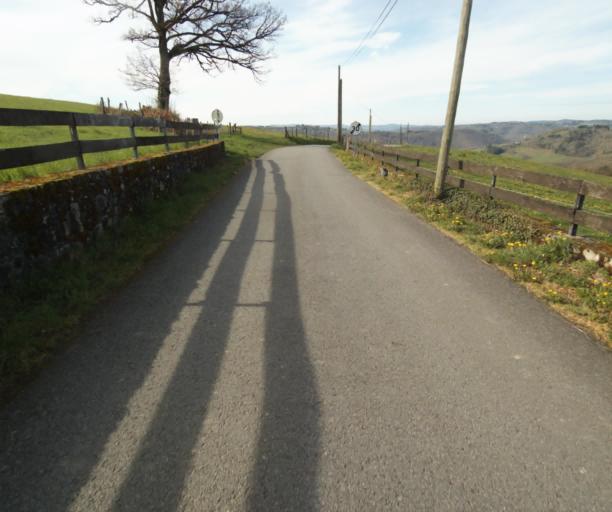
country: FR
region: Limousin
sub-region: Departement de la Correze
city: Correze
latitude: 45.3374
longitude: 1.8292
